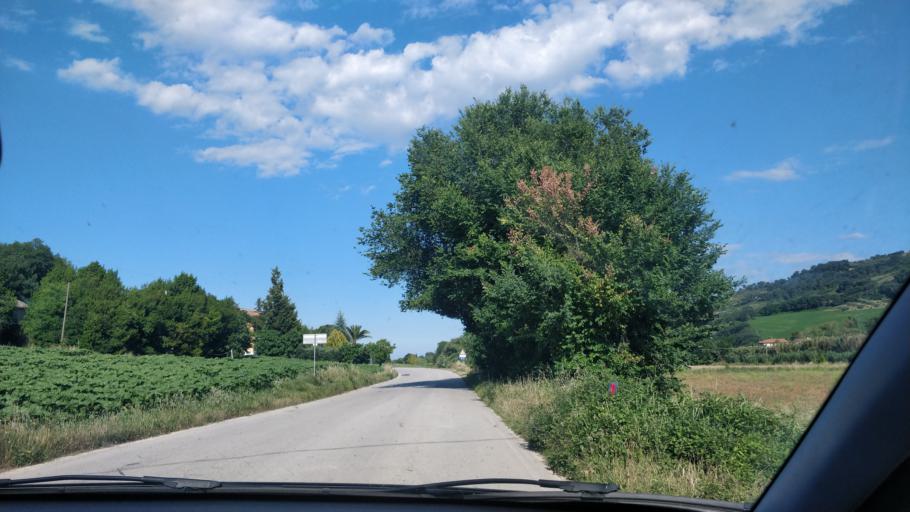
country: IT
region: The Marches
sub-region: Provincia di Ascoli Piceno
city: Massignano
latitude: 43.0371
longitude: 13.8029
